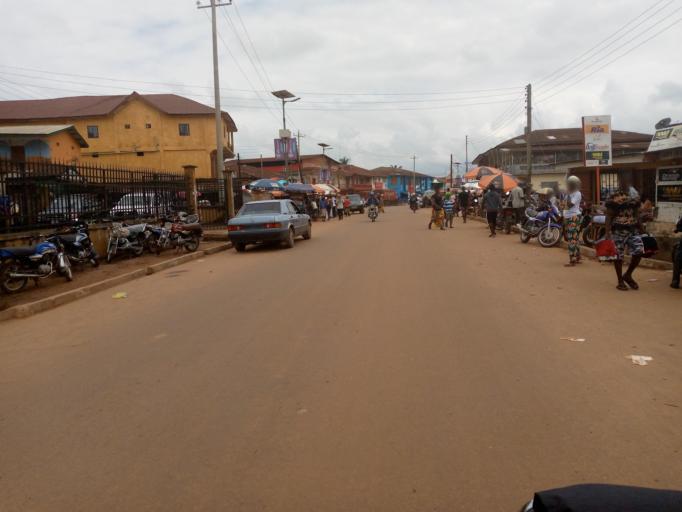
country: SL
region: Eastern Province
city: Kenema
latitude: 7.8734
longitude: -11.1925
